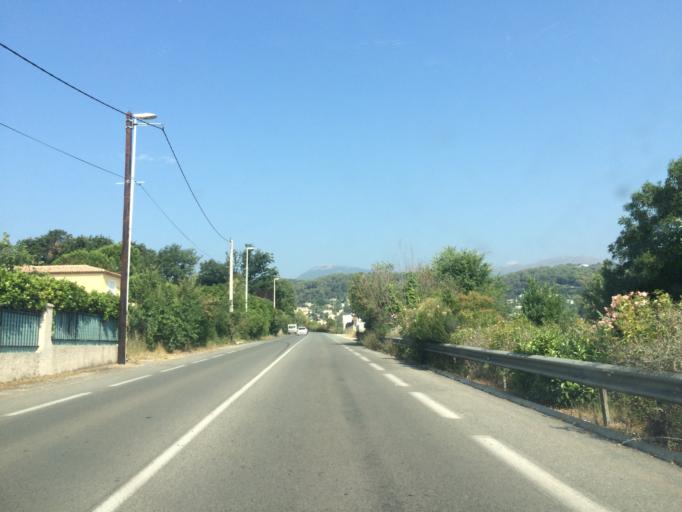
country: FR
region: Provence-Alpes-Cote d'Azur
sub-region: Departement des Alpes-Maritimes
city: La Colle-sur-Loup
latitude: 43.6852
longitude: 7.1122
